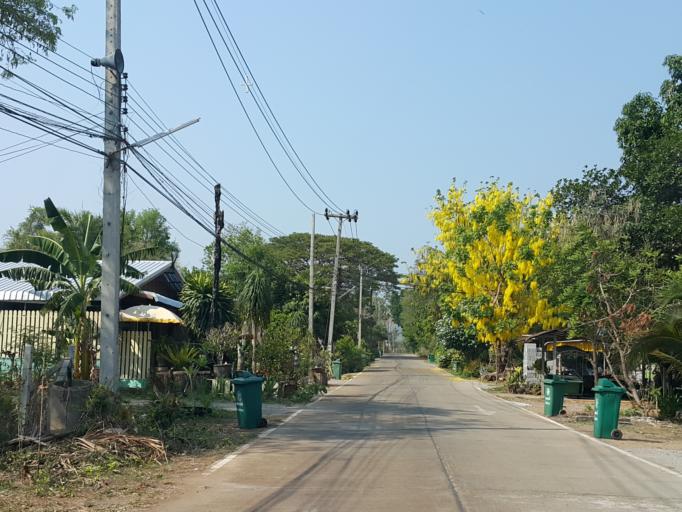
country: TH
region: Kanchanaburi
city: Sai Yok
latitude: 14.1191
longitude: 99.1390
